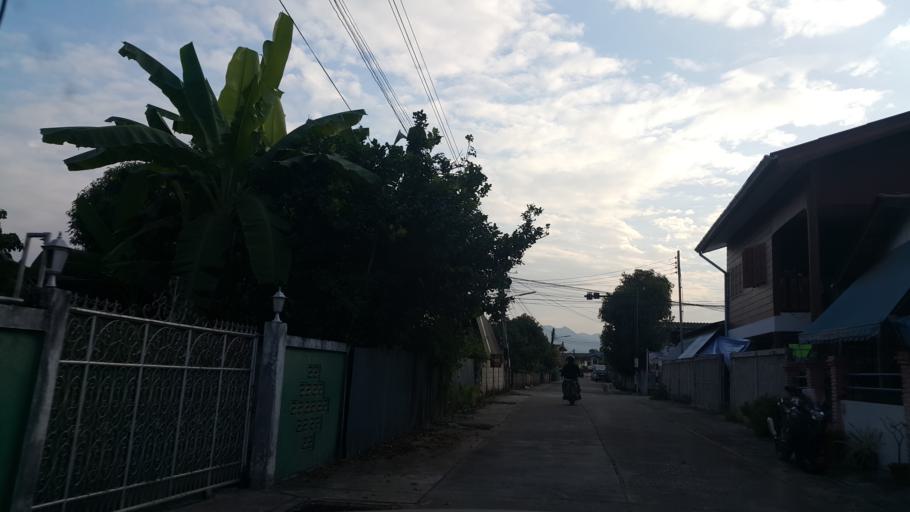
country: TH
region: Lampang
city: Sop Prap
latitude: 17.8841
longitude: 99.3360
